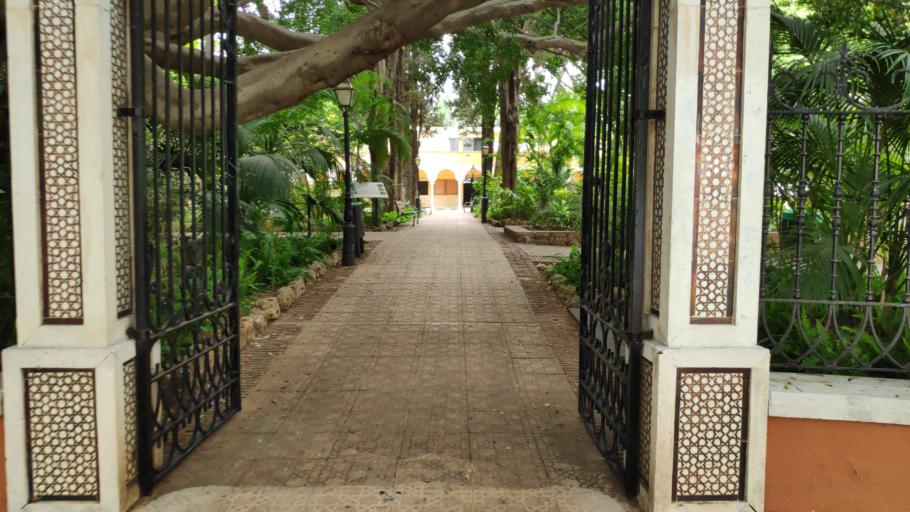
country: ES
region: Andalusia
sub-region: Provincia de Malaga
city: Marbella
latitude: 36.5074
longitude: -4.8913
